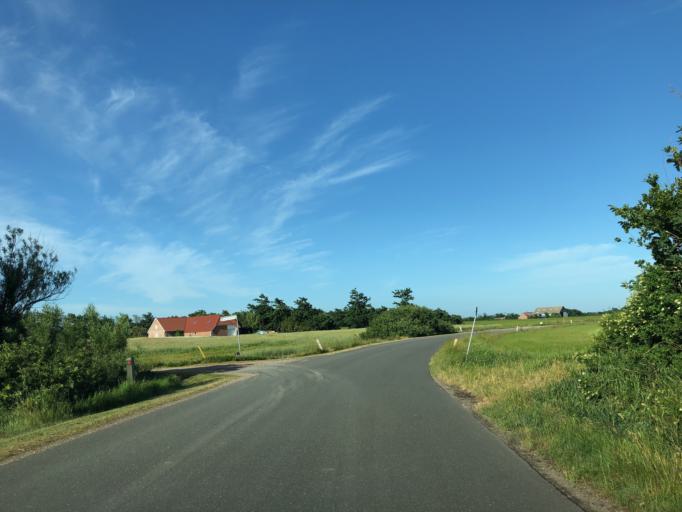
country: DK
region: Central Jutland
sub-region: Holstebro Kommune
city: Ulfborg
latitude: 56.3375
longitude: 8.3015
